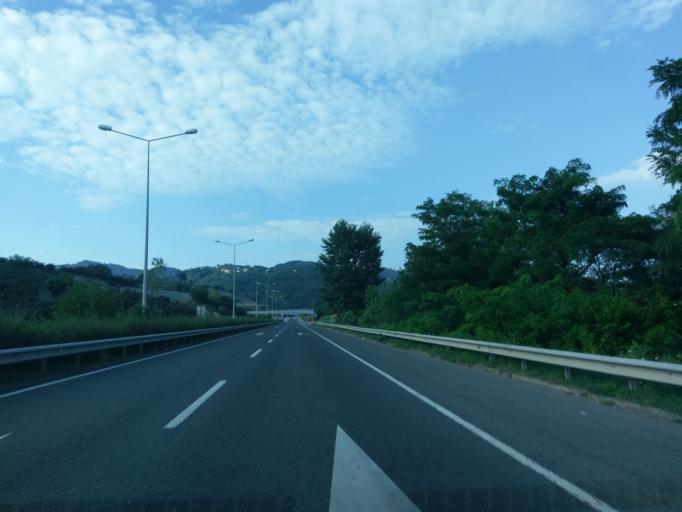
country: TR
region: Ordu
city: Ordu
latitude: 40.9971
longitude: 37.8201
